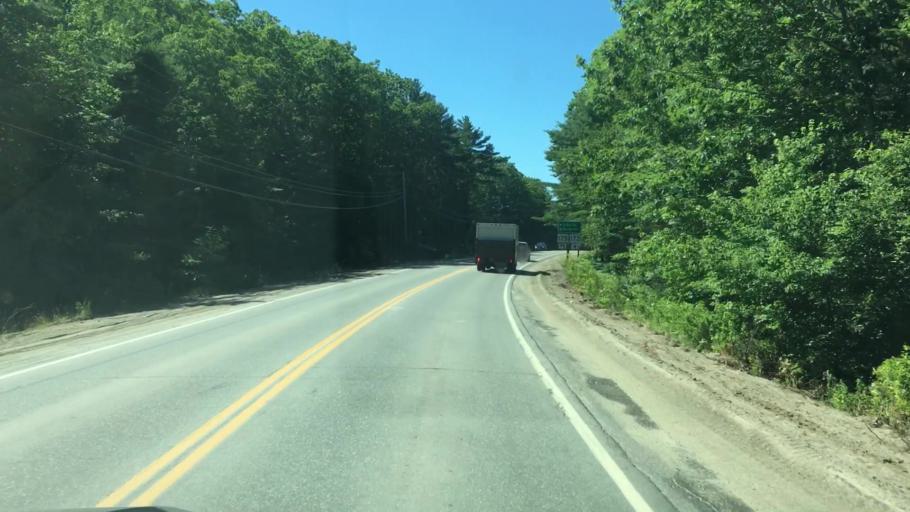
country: US
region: Maine
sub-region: Hancock County
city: Sedgwick
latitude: 44.3815
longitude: -68.5688
